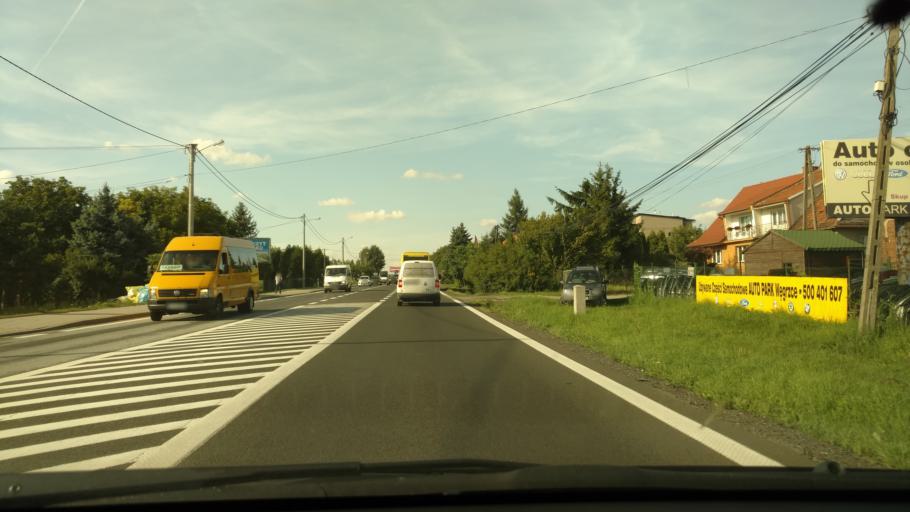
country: PL
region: Lesser Poland Voivodeship
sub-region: Powiat krakowski
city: Michalowice
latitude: 50.1263
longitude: 19.9681
